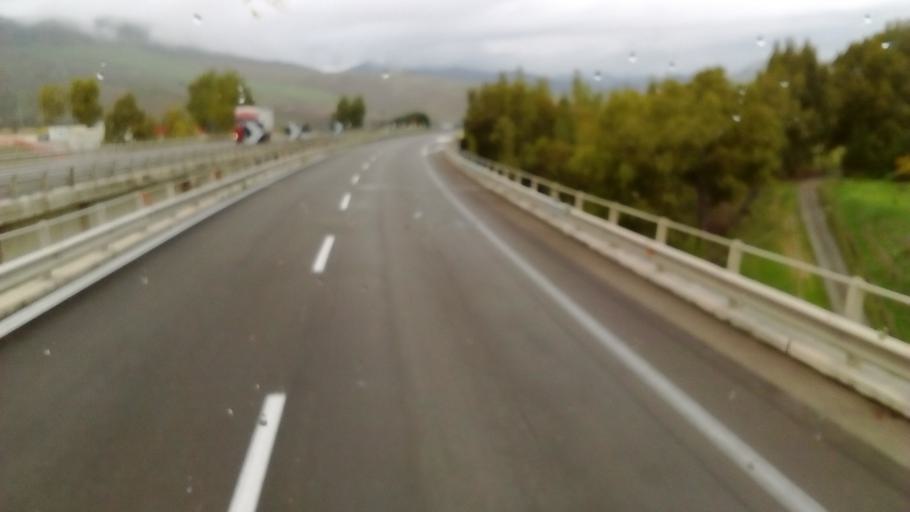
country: IT
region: Sicily
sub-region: Enna
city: Calascibetta
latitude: 37.5692
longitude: 14.2301
